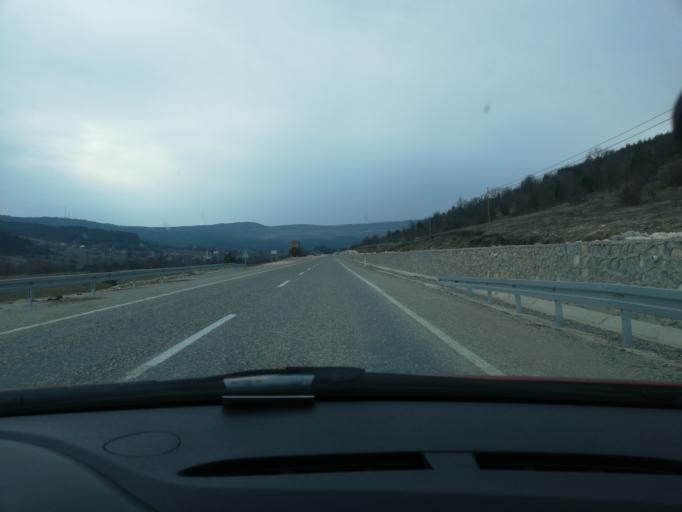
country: TR
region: Kastamonu
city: Pinarbasi
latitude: 41.5963
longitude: 33.1008
